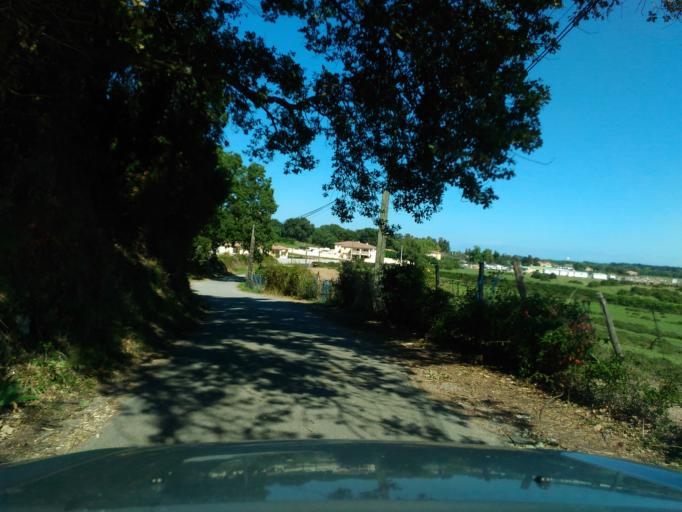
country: FR
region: Corsica
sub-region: Departement de la Haute-Corse
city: Aleria
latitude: 42.1049
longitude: 9.4756
